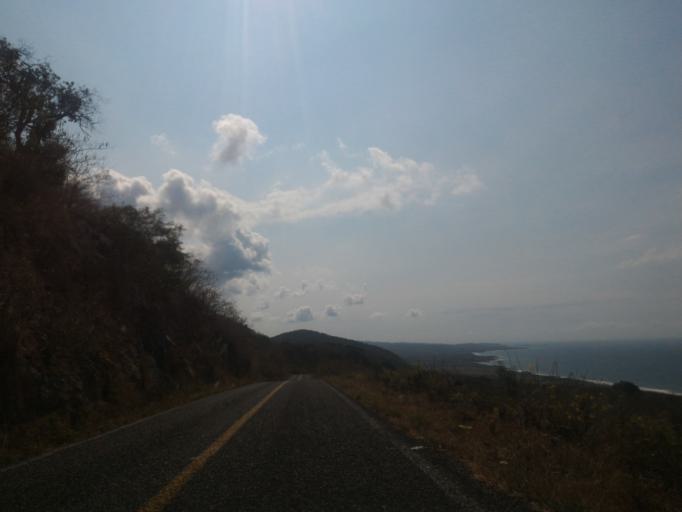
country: MX
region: Michoacan
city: Coahuayana Viejo
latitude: 18.4669
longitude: -103.5566
